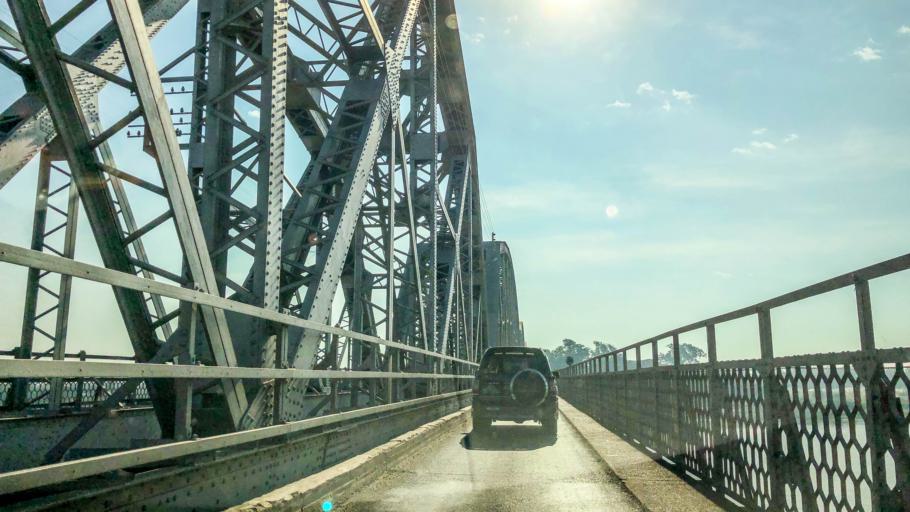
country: MM
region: Sagain
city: Sagaing
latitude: 21.8711
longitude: 95.9925
